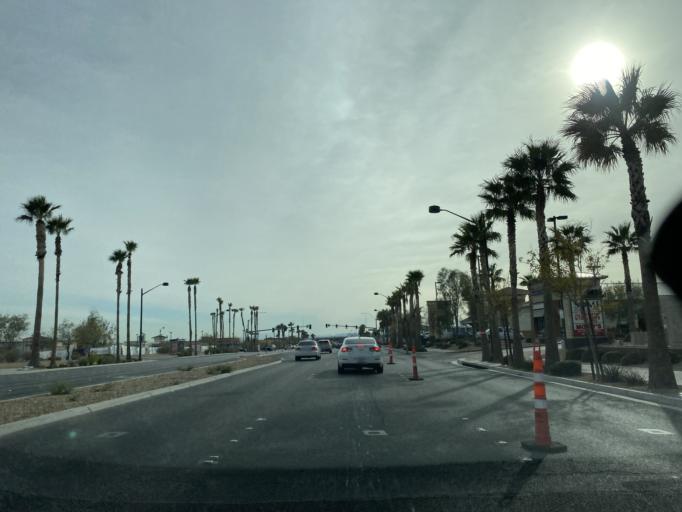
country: US
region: Nevada
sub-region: Clark County
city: Summerlin South
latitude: 36.2861
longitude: -115.2879
